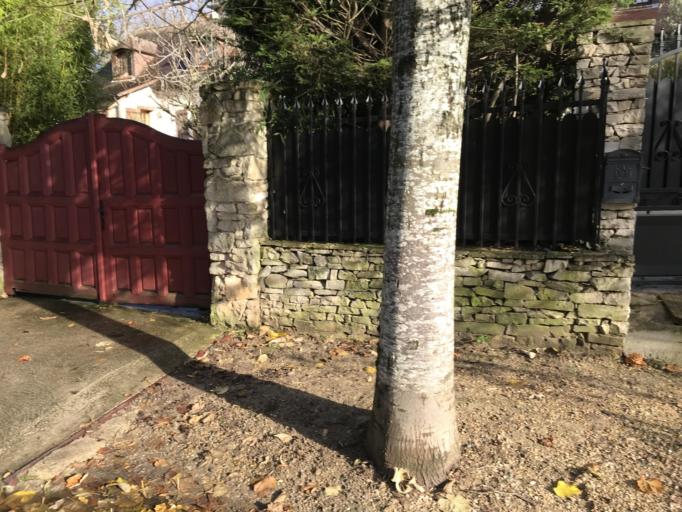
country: FR
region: Ile-de-France
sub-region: Departement de Seine-Saint-Denis
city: Gournay-sur-Marne
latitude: 48.8640
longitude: 2.5698
